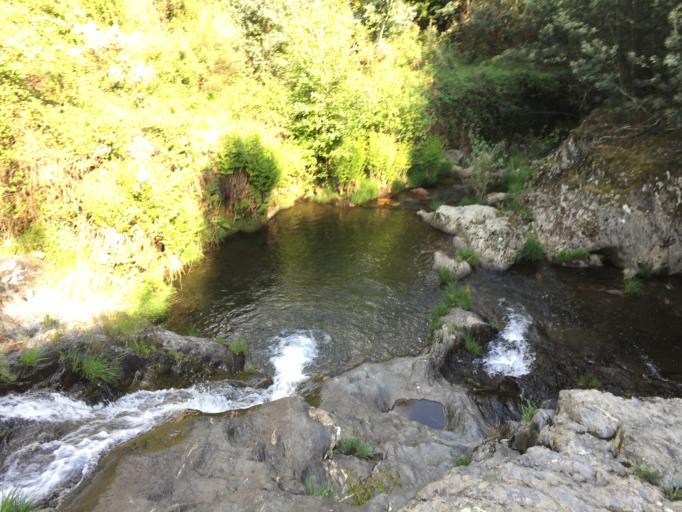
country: PT
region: Coimbra
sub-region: Pampilhosa da Serra
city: Pampilhosa da Serra
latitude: 40.1170
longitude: -7.8696
